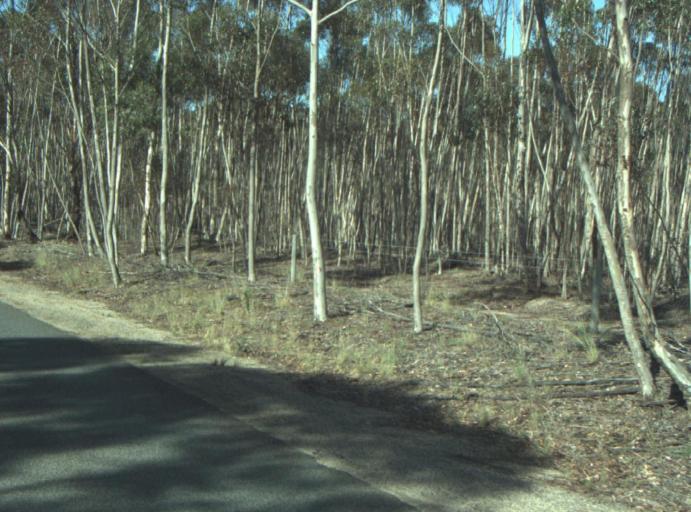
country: AU
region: Victoria
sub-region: Greater Geelong
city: Lara
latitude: -37.9405
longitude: 144.3927
